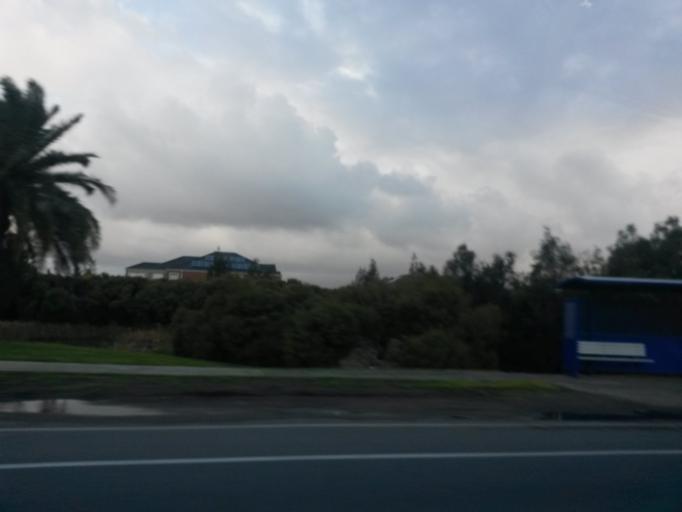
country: AU
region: South Australia
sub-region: Salisbury
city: Ingle Farm
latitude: -34.8052
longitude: 138.6032
